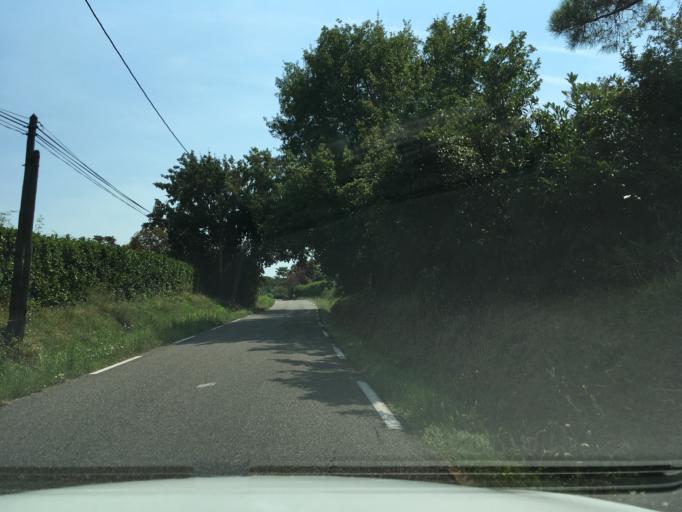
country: FR
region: Midi-Pyrenees
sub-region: Departement du Tarn-et-Garonne
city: Corbarieu
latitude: 43.9805
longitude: 1.3766
